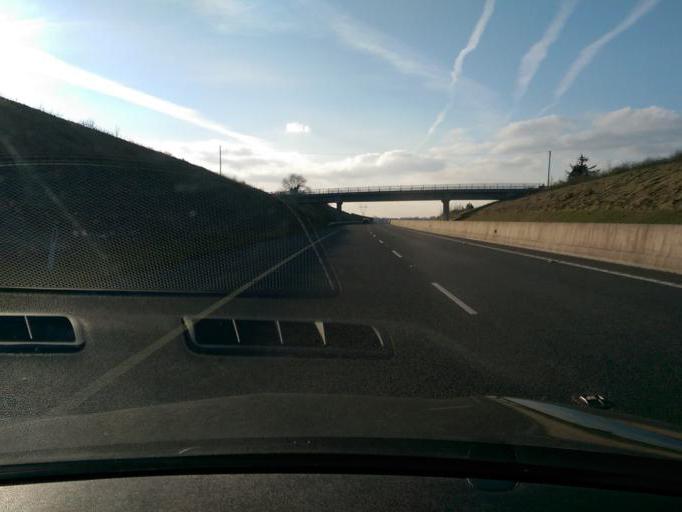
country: IE
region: Leinster
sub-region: Laois
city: Rathdowney
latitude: 52.9127
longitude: -7.5300
